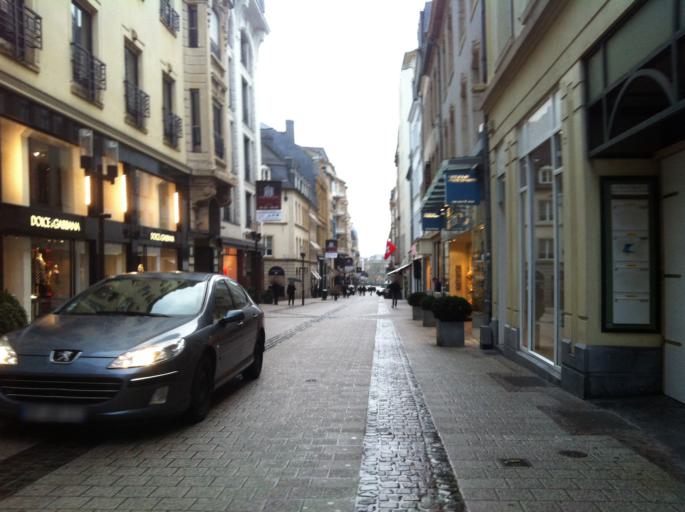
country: LU
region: Luxembourg
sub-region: Canton de Luxembourg
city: Luxembourg
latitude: 49.6118
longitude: 6.1282
